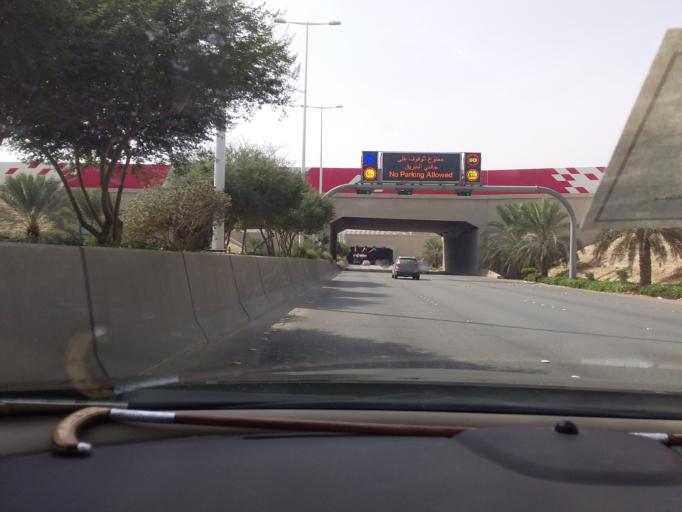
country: SA
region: Ar Riyad
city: Riyadh
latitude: 24.7330
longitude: 46.7335
